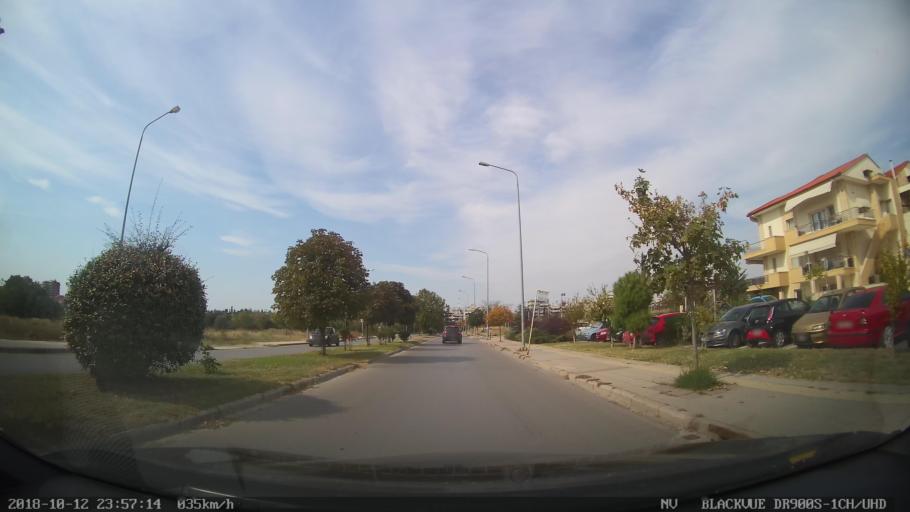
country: GR
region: Central Macedonia
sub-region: Nomos Thessalonikis
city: Pylaia
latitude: 40.6043
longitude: 22.9893
